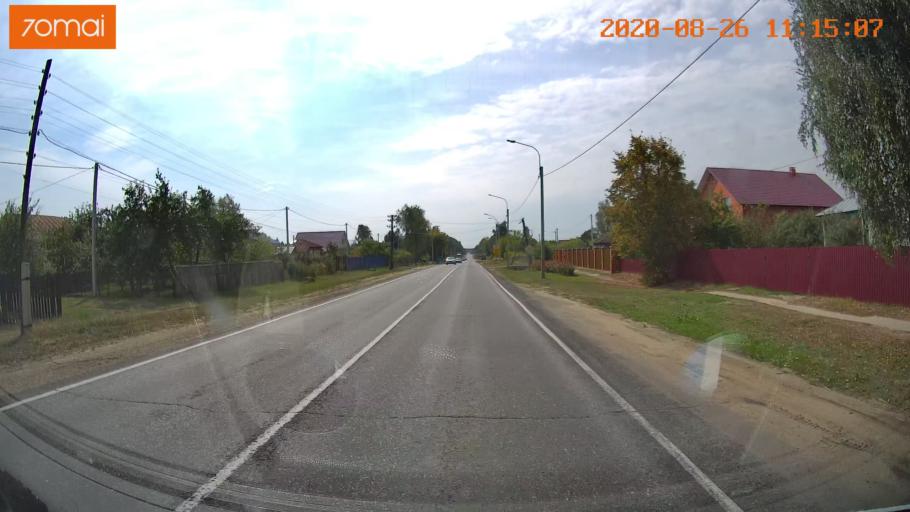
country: RU
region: Rjazan
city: Izhevskoye
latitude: 54.4424
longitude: 41.1154
